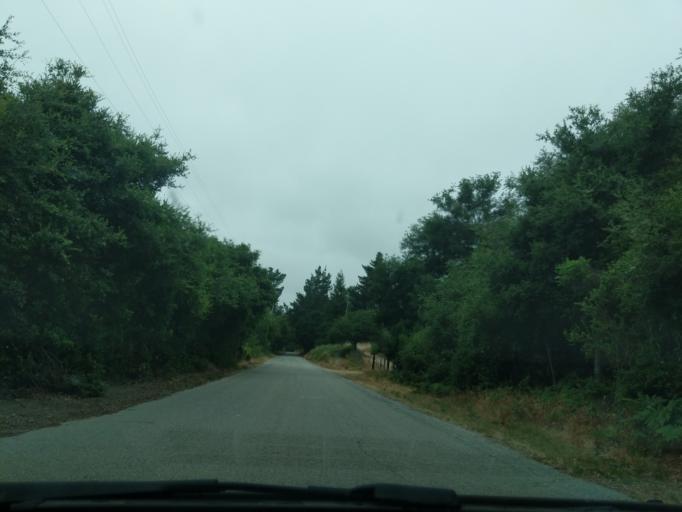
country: US
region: California
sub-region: San Benito County
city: Aromas
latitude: 36.8837
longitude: -121.6206
